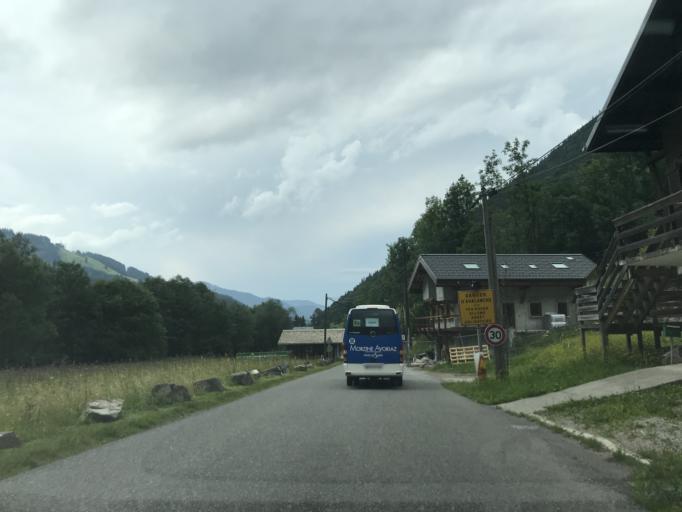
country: FR
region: Rhone-Alpes
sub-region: Departement de la Haute-Savoie
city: Morzine
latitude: 46.1599
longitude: 6.7270
